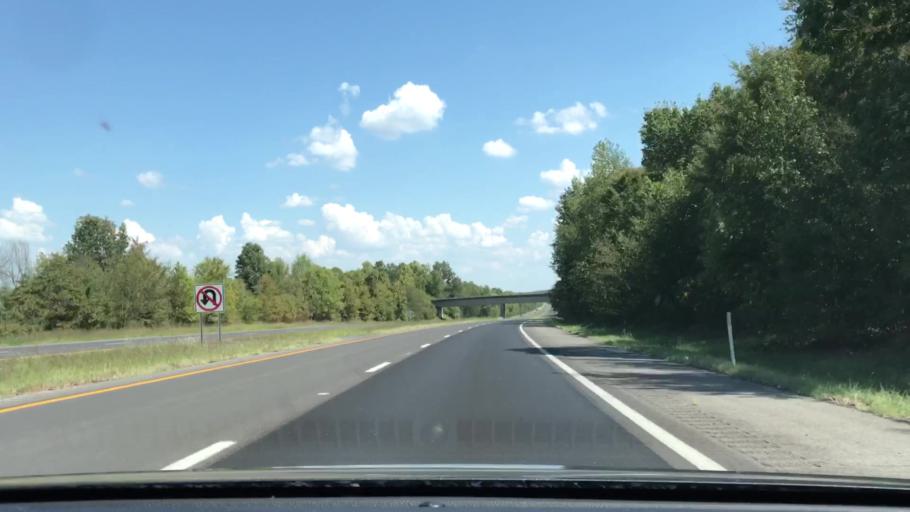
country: US
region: Kentucky
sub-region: Fulton County
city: Fulton
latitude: 36.5869
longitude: -88.8189
